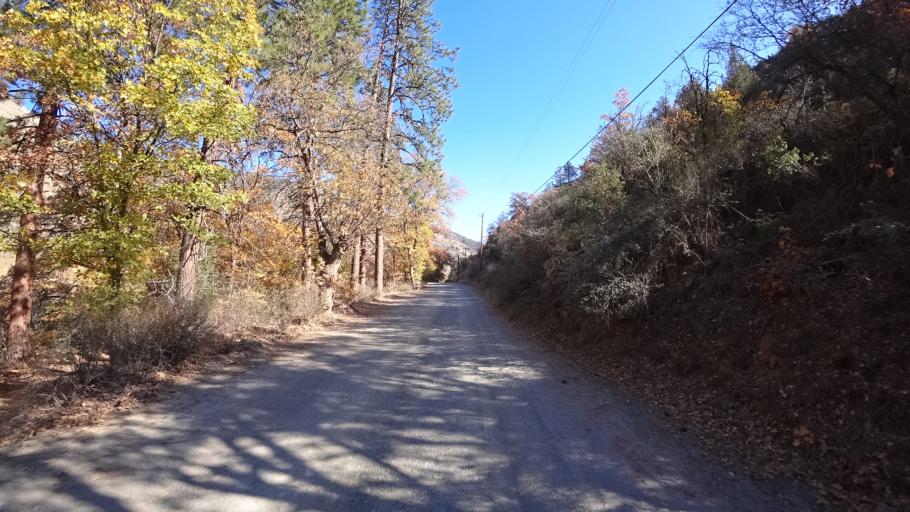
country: US
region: California
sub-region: Siskiyou County
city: Yreka
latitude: 41.8328
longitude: -122.6230
